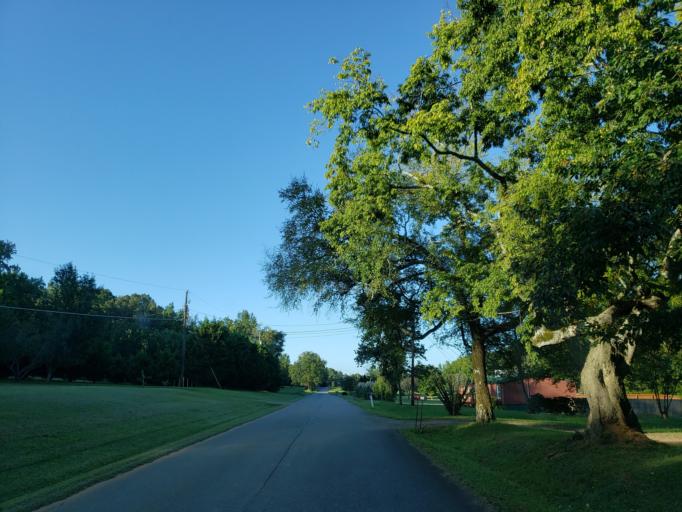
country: US
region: Georgia
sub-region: Bartow County
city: Rydal
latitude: 34.2985
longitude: -84.7346
